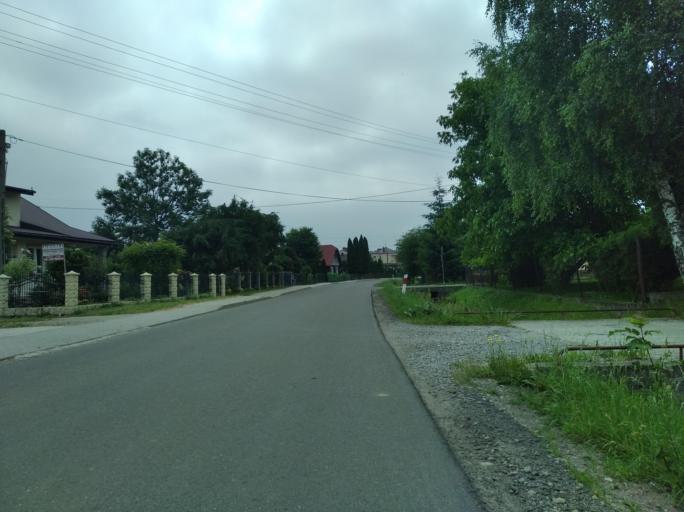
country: PL
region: Subcarpathian Voivodeship
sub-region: Powiat sanocki
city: Besko
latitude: 49.5928
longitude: 21.9399
